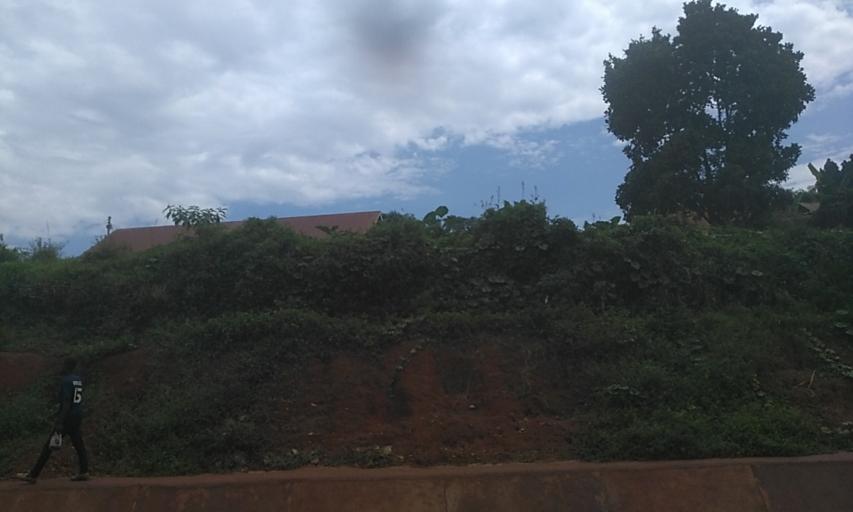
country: UG
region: Central Region
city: Kampala Central Division
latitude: 0.3357
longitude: 32.5298
